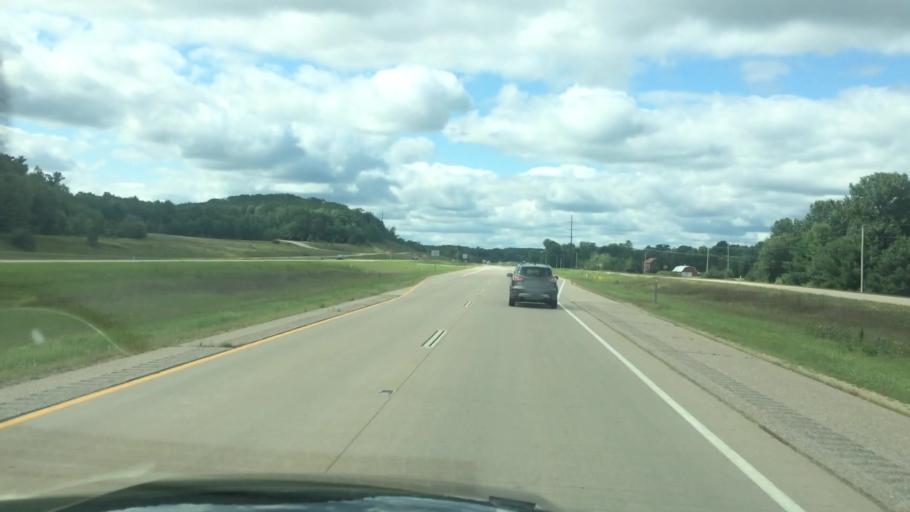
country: US
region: Wisconsin
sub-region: Waupaca County
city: King
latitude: 44.3719
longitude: -89.1511
